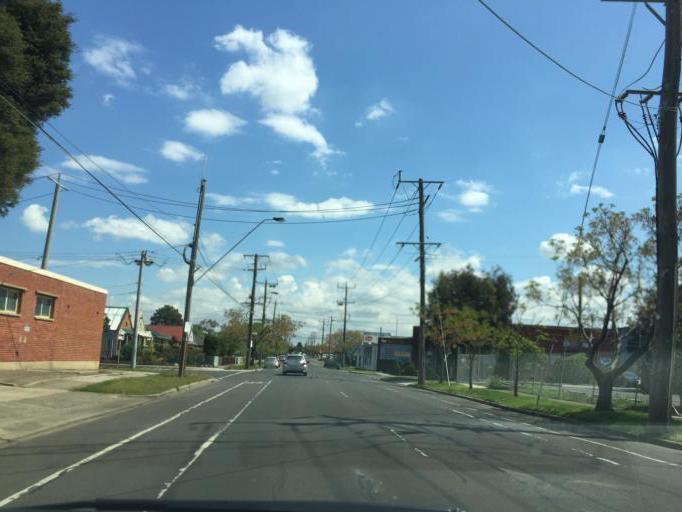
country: AU
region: Victoria
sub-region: Maribyrnong
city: Maidstone
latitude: -37.7822
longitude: 144.8753
